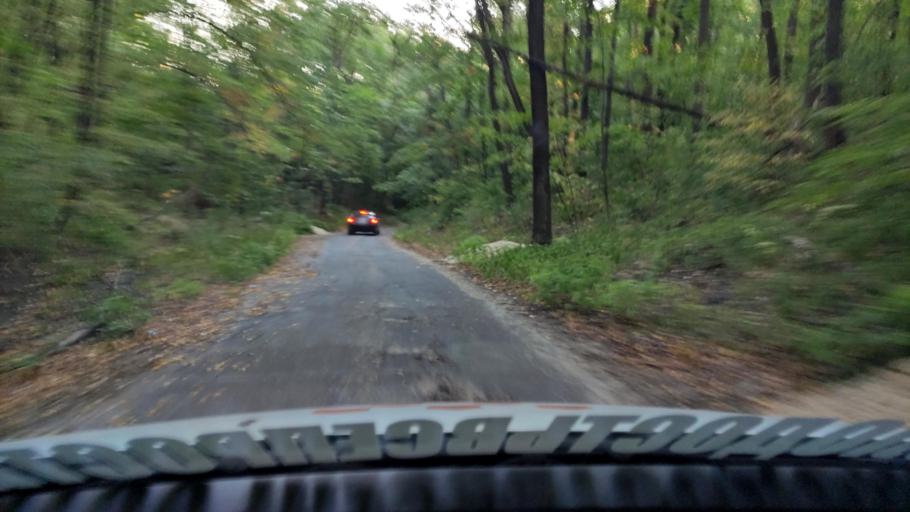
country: RU
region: Voronezj
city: Podgornoye
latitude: 51.7426
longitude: 39.2241
